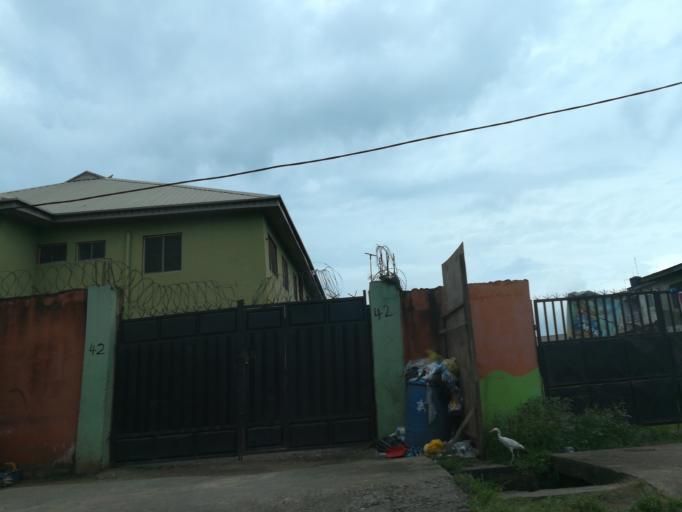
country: NG
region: Lagos
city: Agege
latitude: 6.6091
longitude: 3.3248
